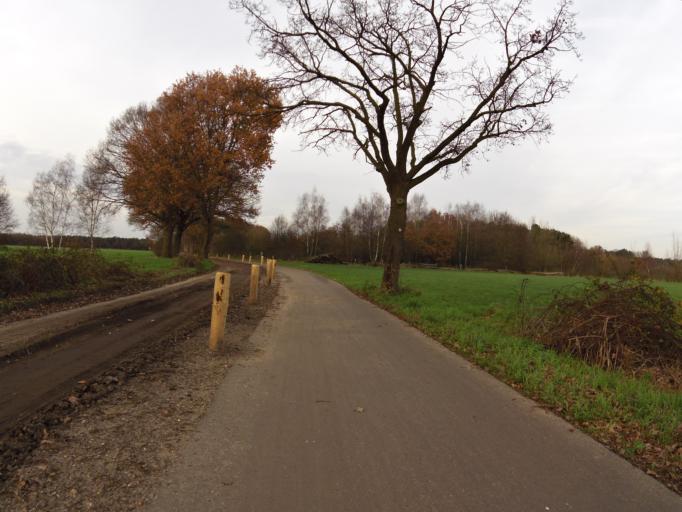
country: NL
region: North Brabant
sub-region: Gemeente Uden
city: Uden
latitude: 51.6978
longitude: 5.6004
